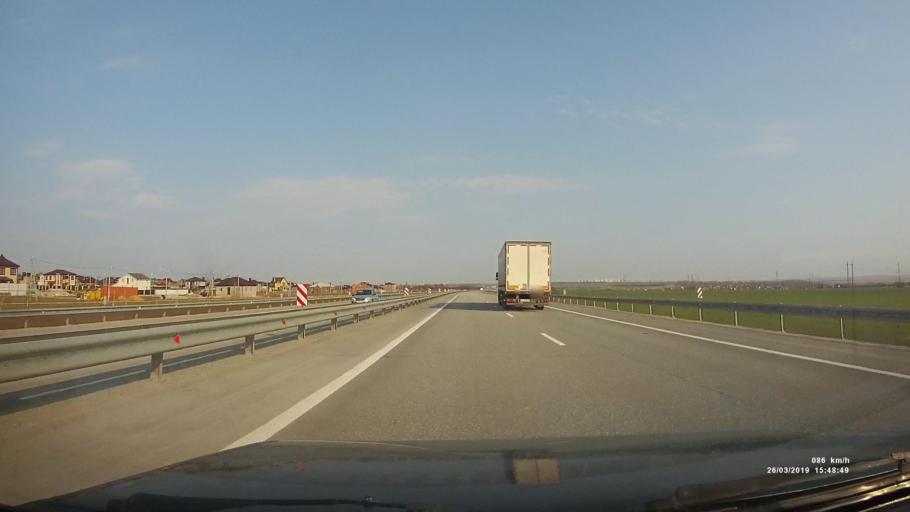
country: RU
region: Rostov
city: Chaltyr
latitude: 47.2780
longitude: 39.4584
